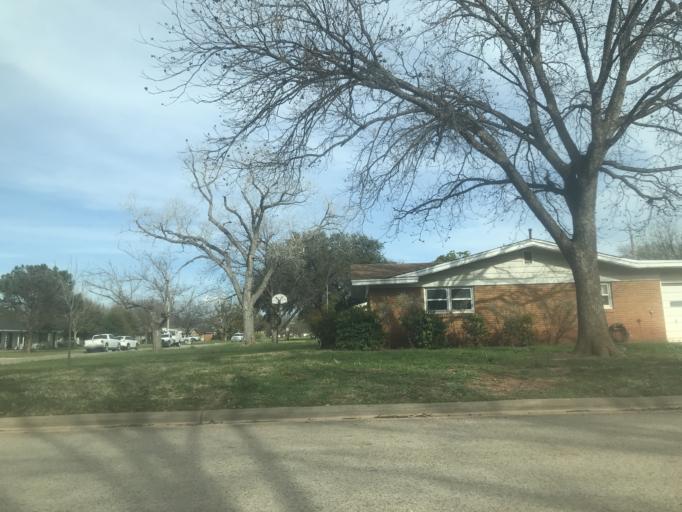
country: US
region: Texas
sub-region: Taylor County
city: Abilene
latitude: 32.4243
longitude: -99.7724
